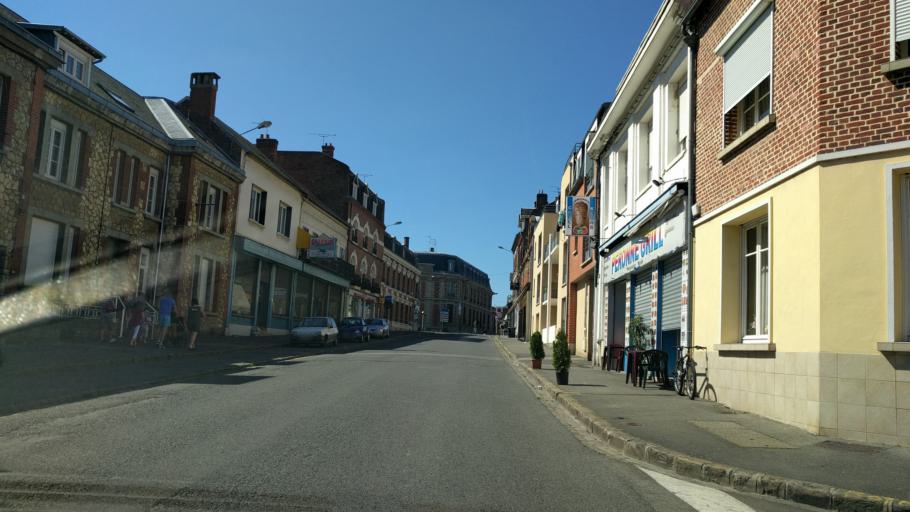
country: FR
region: Picardie
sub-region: Departement de la Somme
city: Peronne
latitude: 49.9298
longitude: 2.9376
